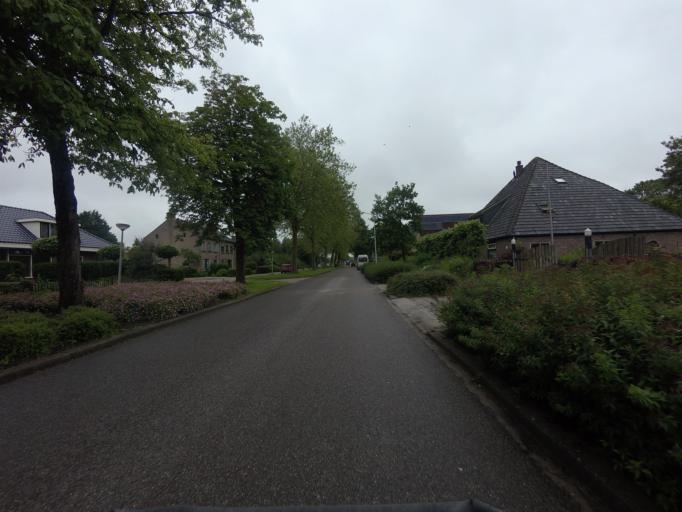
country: NL
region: North Holland
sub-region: Gemeente Opmeer
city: Opmeer
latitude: 52.7578
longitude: 4.8986
